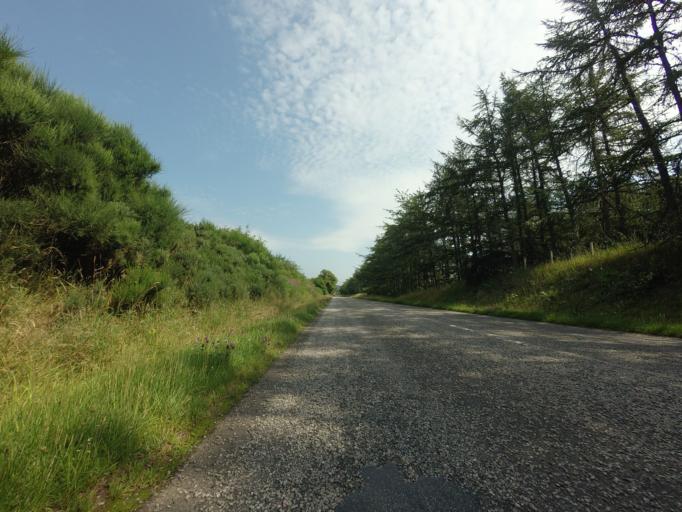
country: GB
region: Scotland
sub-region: Highland
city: Evanton
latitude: 57.9157
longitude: -4.3875
